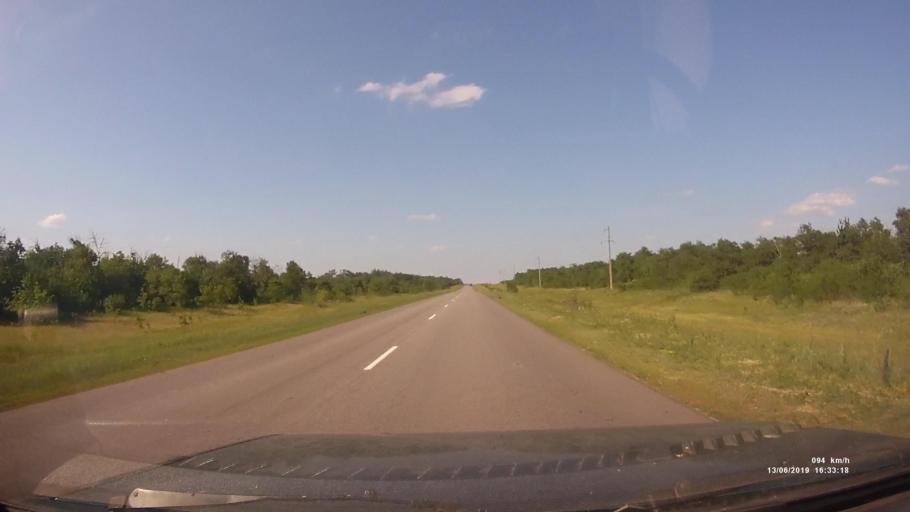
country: RU
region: Rostov
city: Kazanskaya
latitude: 49.8590
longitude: 41.2790
